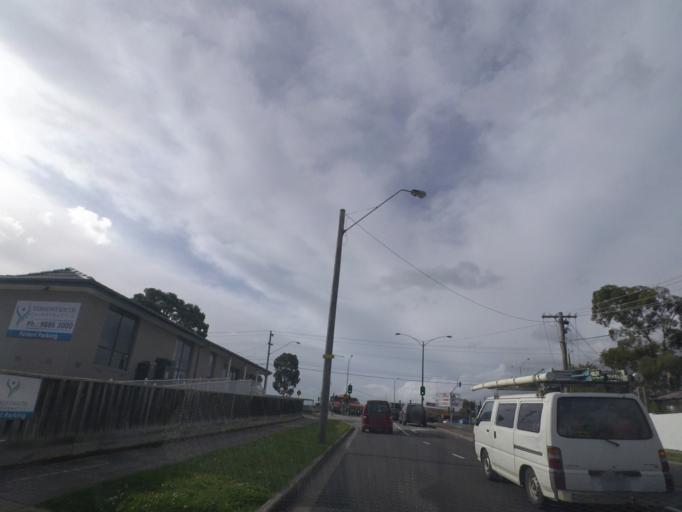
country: AU
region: Victoria
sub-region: Whitehorse
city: Vermont South
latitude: -37.8573
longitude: 145.1829
